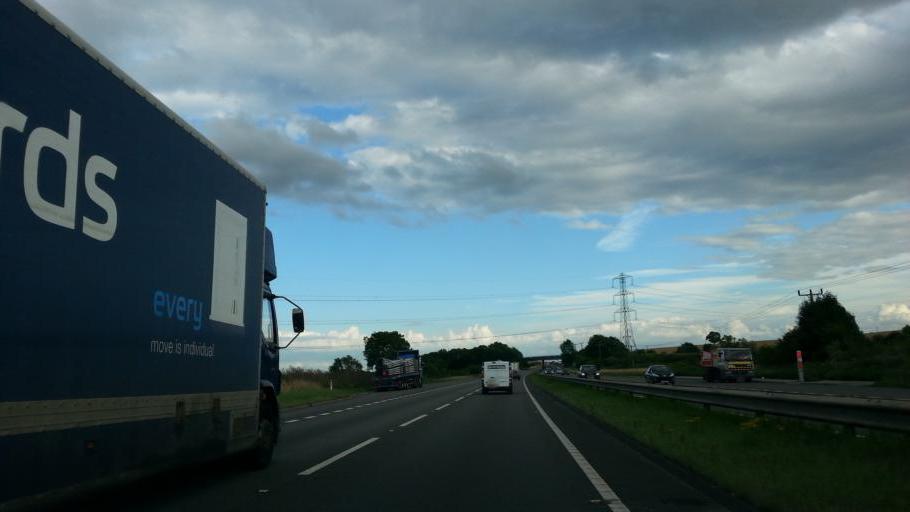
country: GB
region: England
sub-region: Nottinghamshire
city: Tuxford
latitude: 53.1873
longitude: -0.8292
